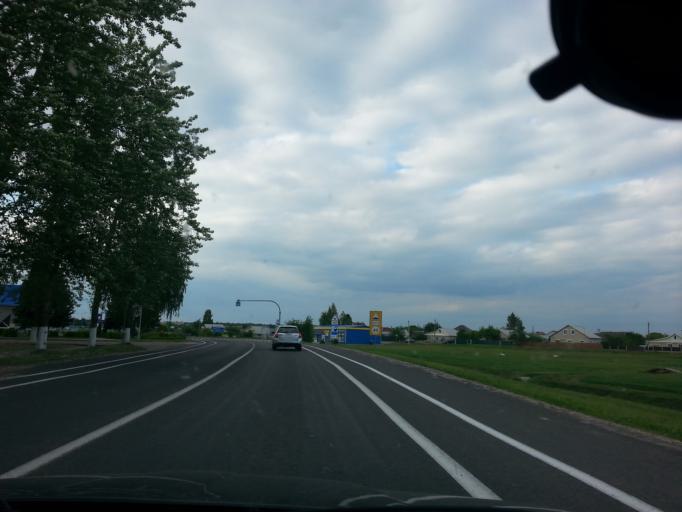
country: BY
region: Minsk
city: Myadzyel
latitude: 54.8752
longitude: 26.9412
